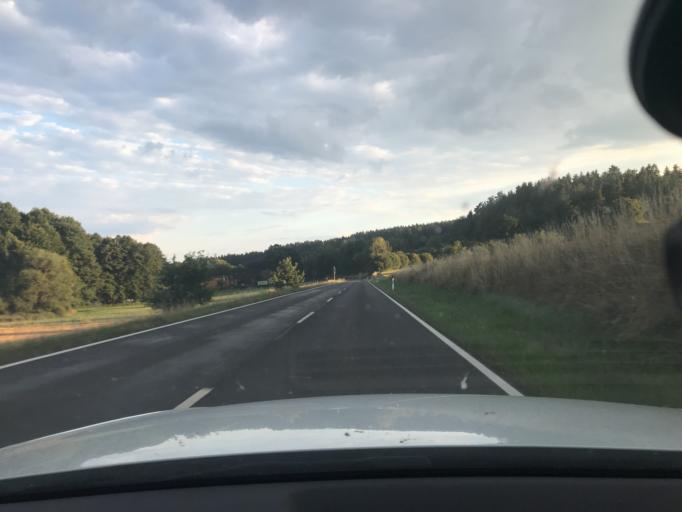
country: DE
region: Bavaria
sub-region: Upper Franconia
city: Pegnitz
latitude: 49.7515
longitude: 11.6067
